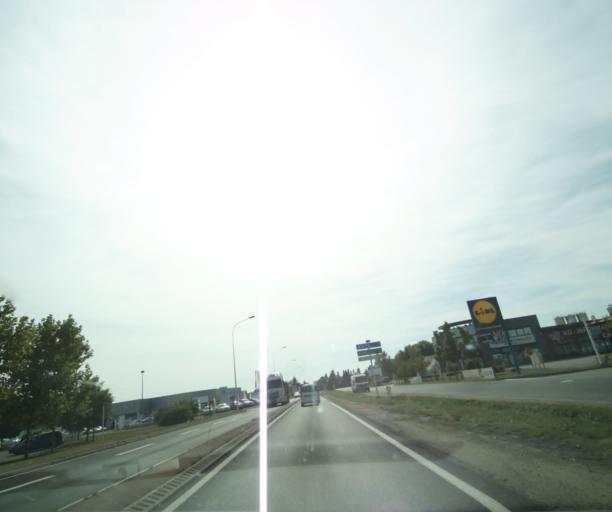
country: FR
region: Auvergne
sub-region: Departement de l'Allier
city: Saint-Remy-en-Rollat
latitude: 46.1565
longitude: 3.3933
